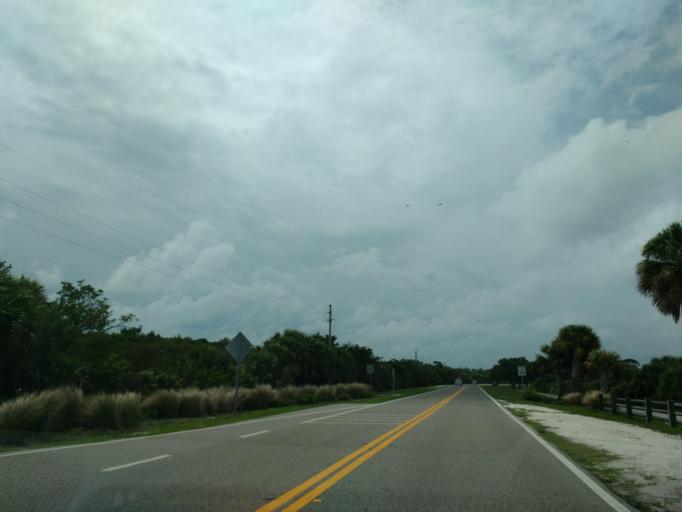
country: US
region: Florida
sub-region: Pinellas County
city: Tierra Verde
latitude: 27.6274
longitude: -82.7165
